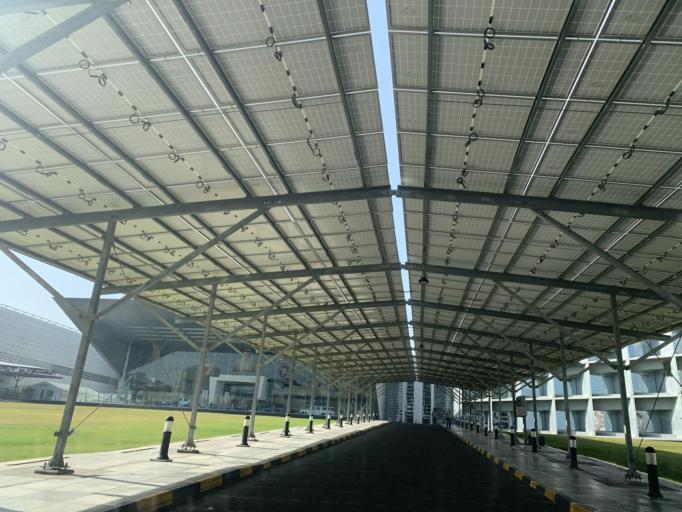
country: BH
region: Muharraq
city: Al Muharraq
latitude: 26.2634
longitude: 50.6003
